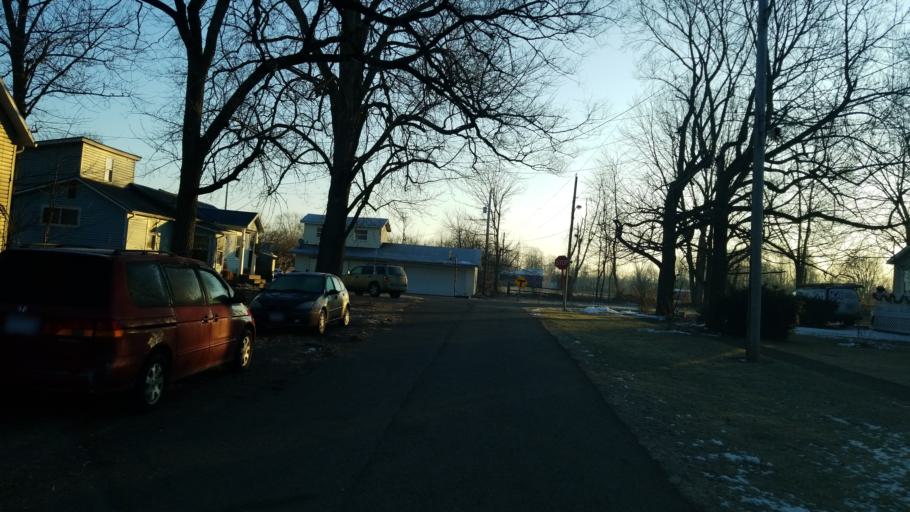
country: US
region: Ohio
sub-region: Morrow County
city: Mount Gilead
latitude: 40.5576
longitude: -82.8598
